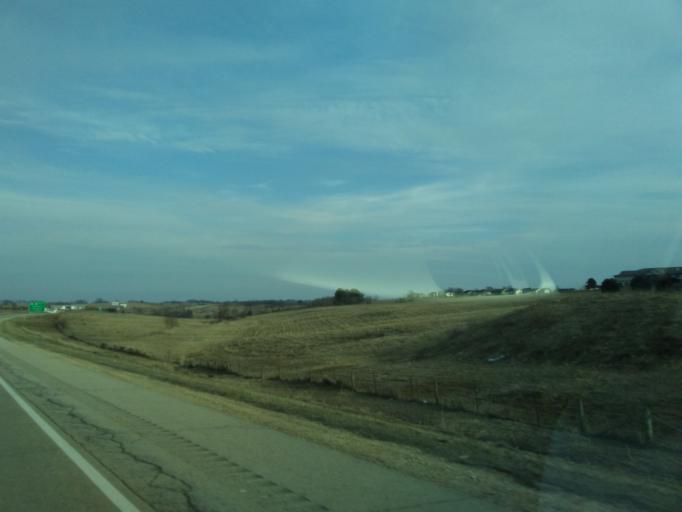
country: US
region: Wisconsin
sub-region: Iowa County
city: Dodgeville
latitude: 42.9724
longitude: -90.1245
